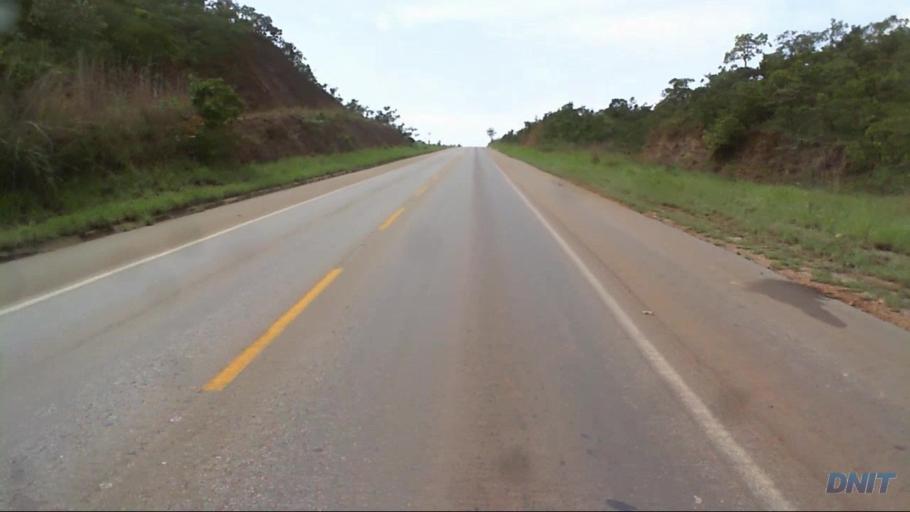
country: BR
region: Goias
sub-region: Barro Alto
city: Barro Alto
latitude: -15.1677
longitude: -48.7975
